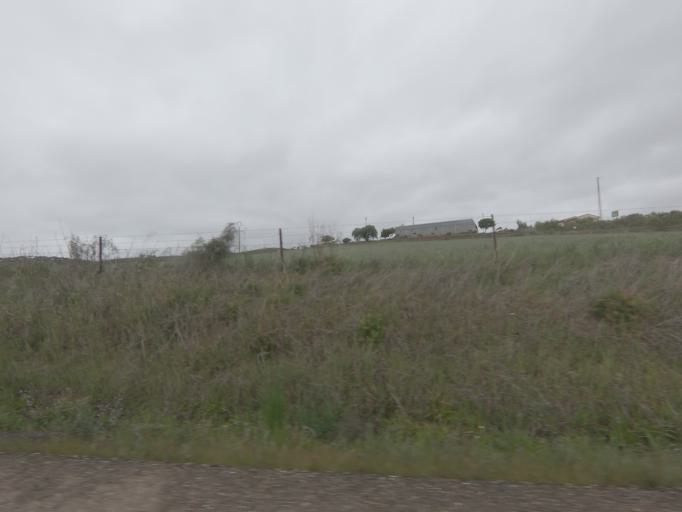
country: ES
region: Extremadura
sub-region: Provincia de Badajoz
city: La Roca de la Sierra
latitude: 39.1091
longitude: -6.6981
